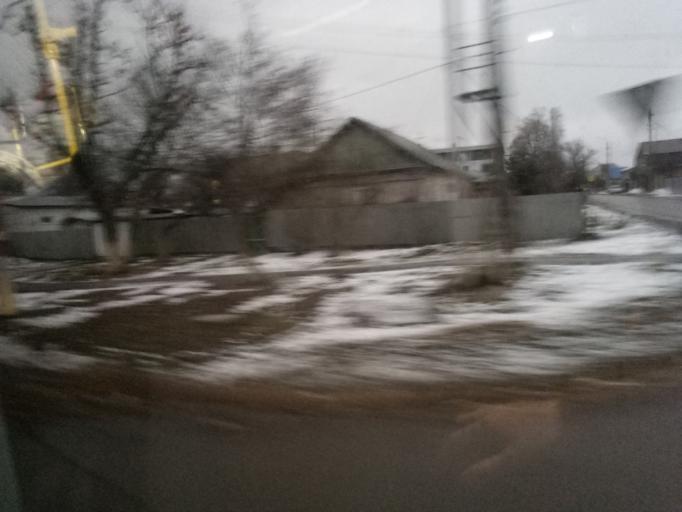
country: RU
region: Tula
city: Tula
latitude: 54.2076
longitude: 37.5653
